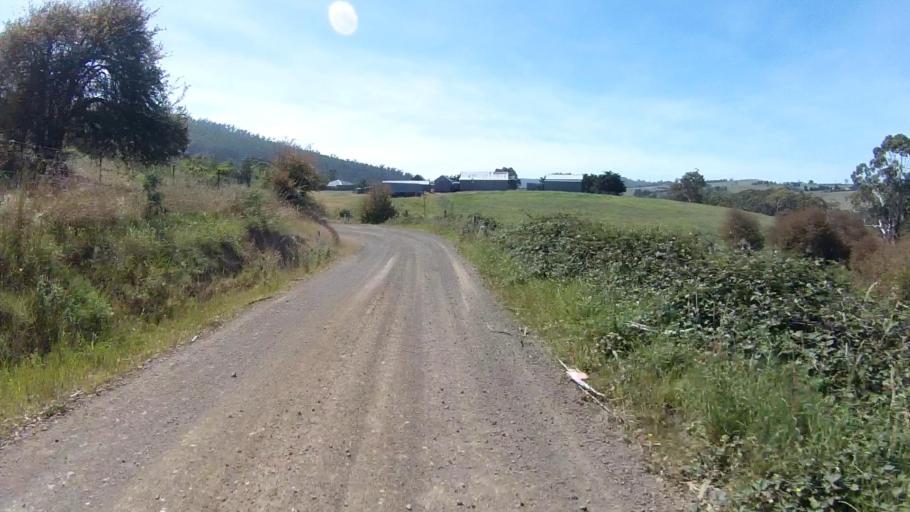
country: AU
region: Tasmania
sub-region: Sorell
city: Sorell
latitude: -42.7474
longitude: 147.6130
